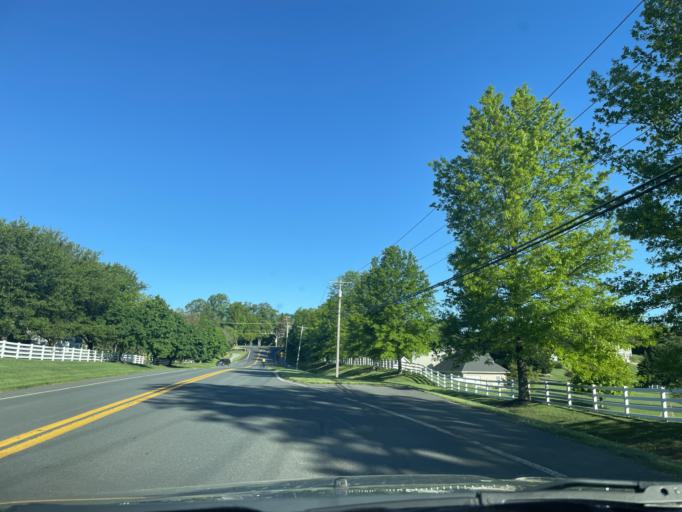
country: US
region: Maryland
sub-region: Carroll County
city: Mount Airy
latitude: 39.4077
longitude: -77.1258
